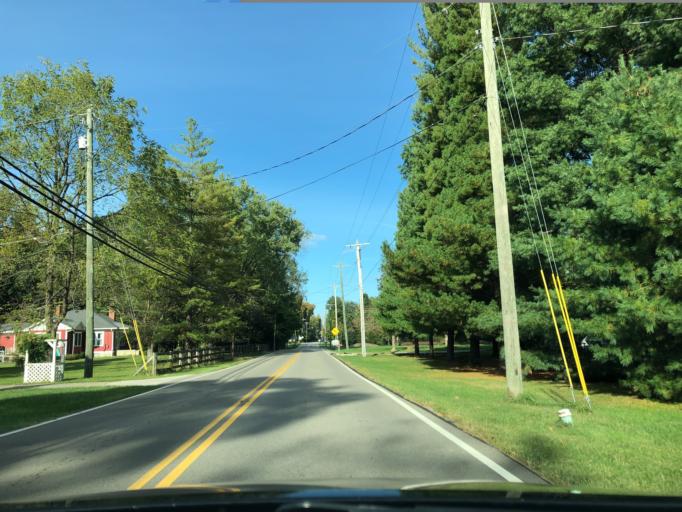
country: US
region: Ohio
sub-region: Hamilton County
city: Loveland
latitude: 39.2569
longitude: -84.2644
